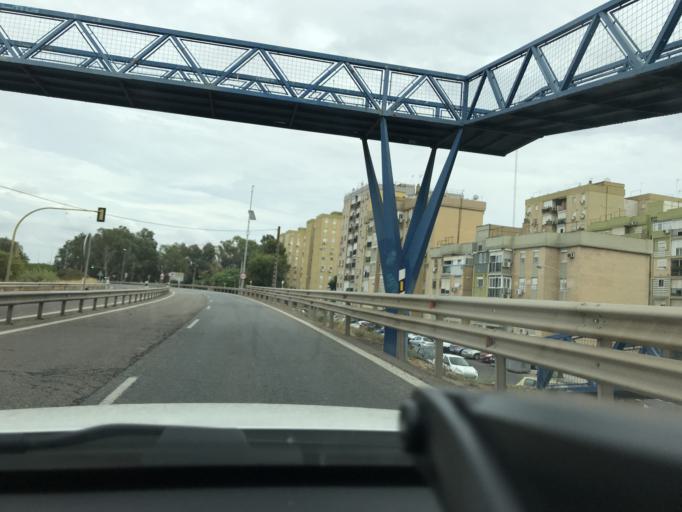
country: ES
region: Andalusia
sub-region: Provincia de Sevilla
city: Sevilla
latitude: 37.4248
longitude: -5.9610
